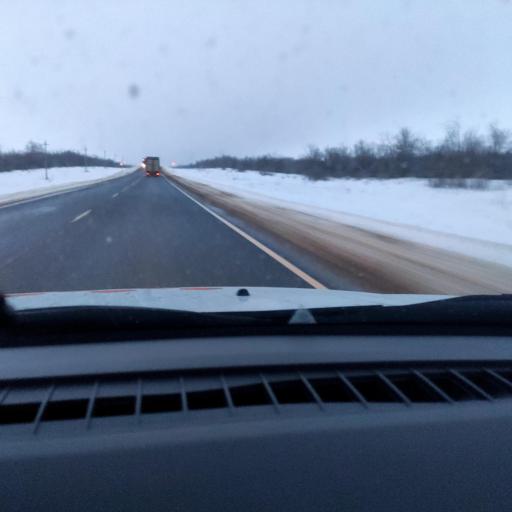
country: RU
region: Saratov
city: Perelyub
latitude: 52.1663
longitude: 50.7976
